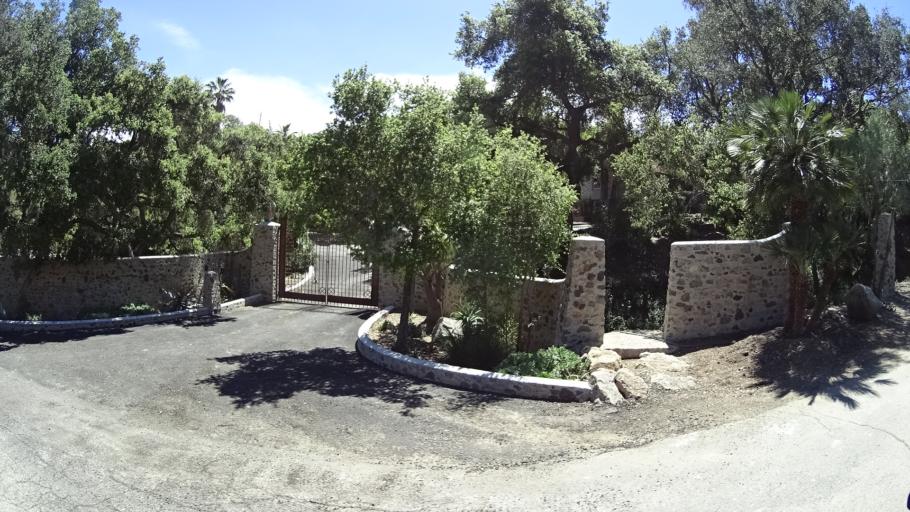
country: US
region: California
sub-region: Ventura County
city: Thousand Oaks
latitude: 34.1667
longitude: -118.8452
